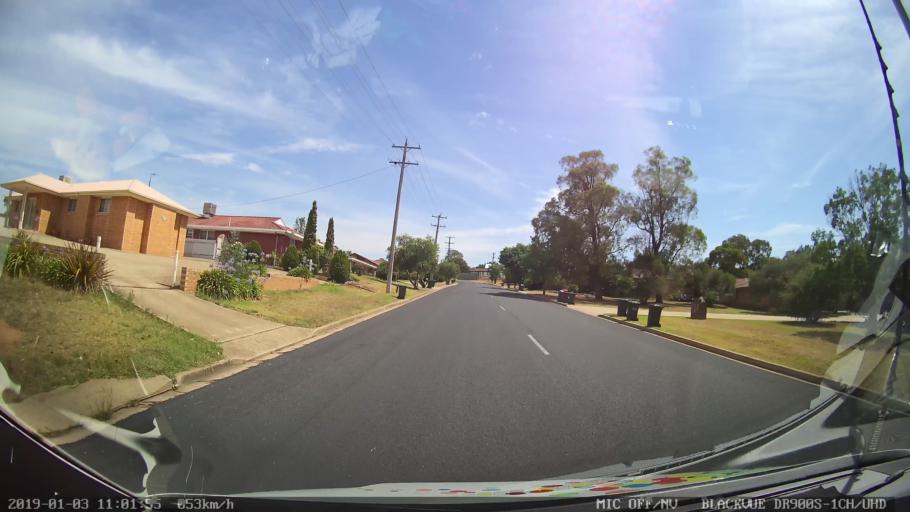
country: AU
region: New South Wales
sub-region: Young
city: Young
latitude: -34.3016
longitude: 148.2992
